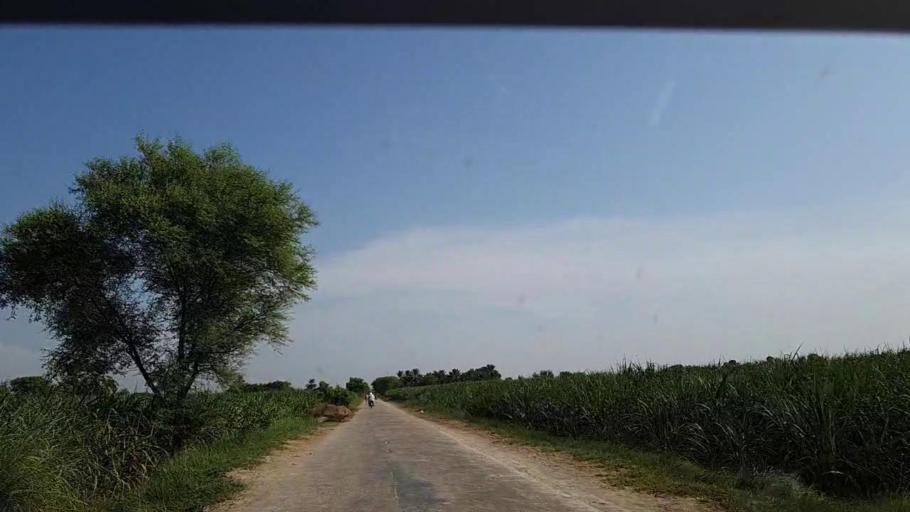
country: PK
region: Sindh
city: Adilpur
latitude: 27.9401
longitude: 69.2536
